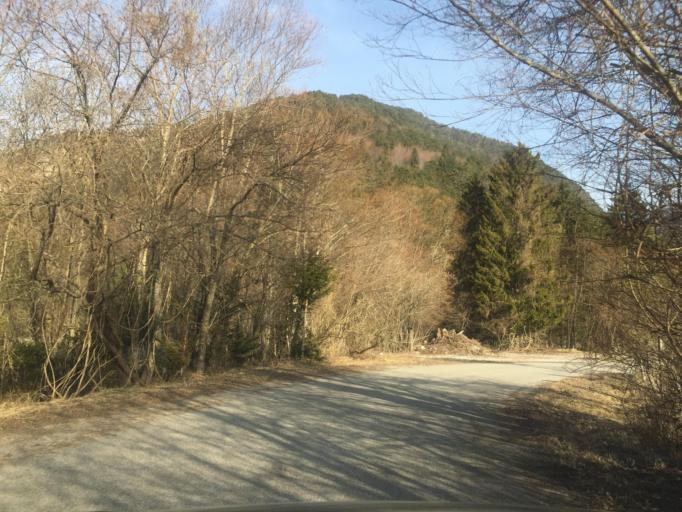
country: IT
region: Friuli Venezia Giulia
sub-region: Provincia di Udine
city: Malborghetto
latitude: 46.5022
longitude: 13.3963
